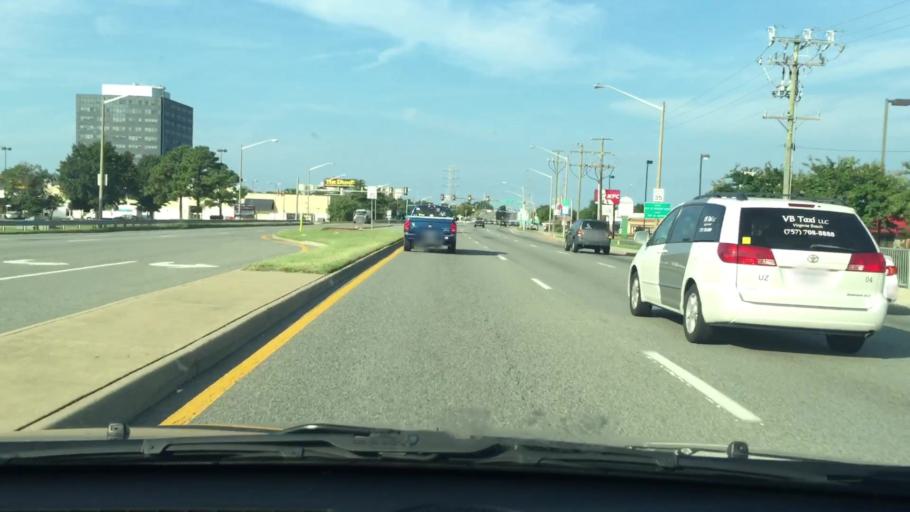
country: US
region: Virginia
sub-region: City of Newport News
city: Newport News
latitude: 37.0215
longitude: -76.4404
